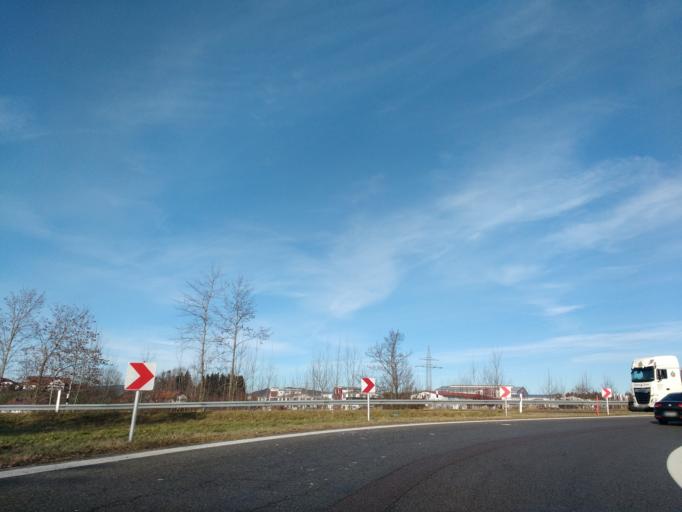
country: DE
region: Bavaria
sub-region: Swabia
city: Waltenhofen
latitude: 47.6810
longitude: 10.3031
